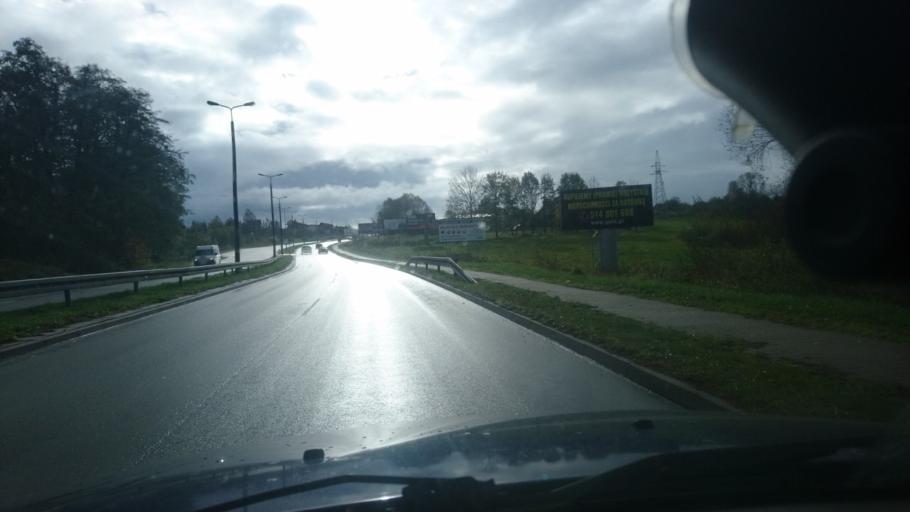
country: PL
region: Silesian Voivodeship
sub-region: Bielsko-Biala
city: Bielsko-Biala
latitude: 49.8326
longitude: 19.0100
